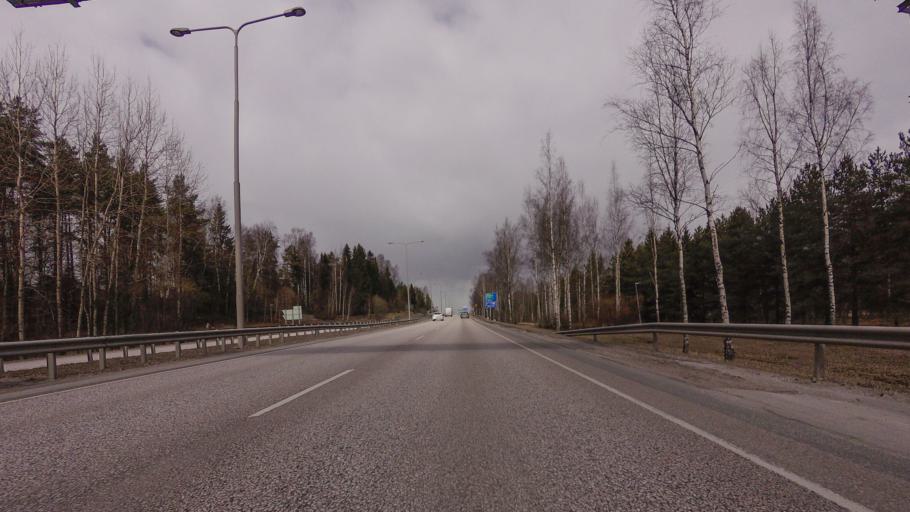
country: FI
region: Uusimaa
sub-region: Helsinki
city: Teekkarikylae
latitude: 60.2806
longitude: 24.8674
